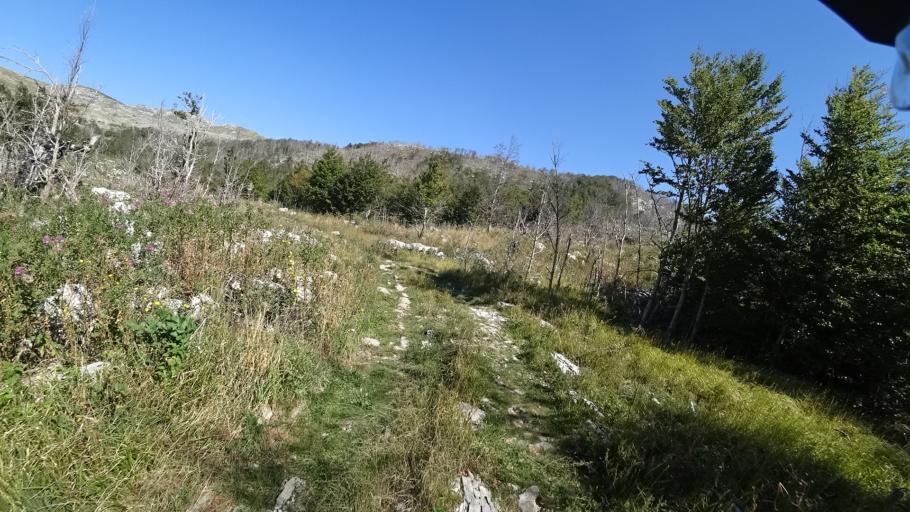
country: HR
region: Splitsko-Dalmatinska
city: Hrvace
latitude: 43.9141
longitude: 16.6106
